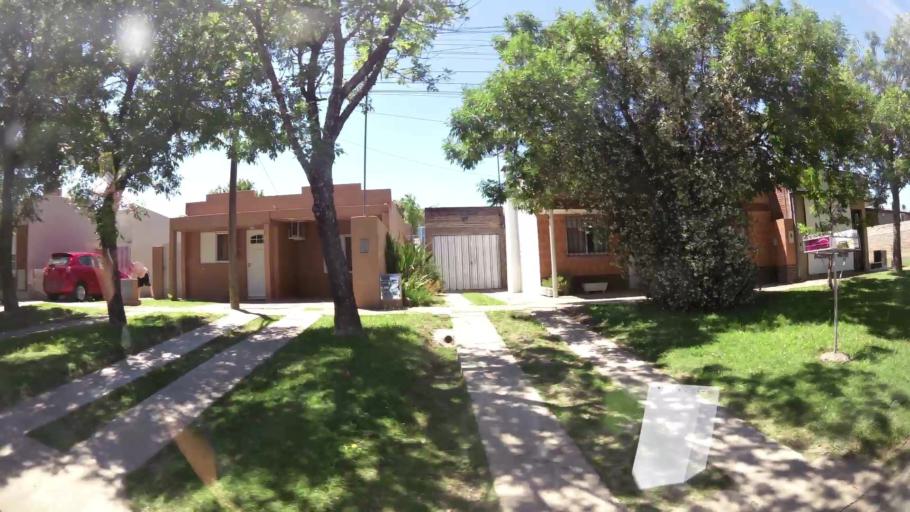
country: AR
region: Santa Fe
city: Esperanza
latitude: -31.3991
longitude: -61.0859
